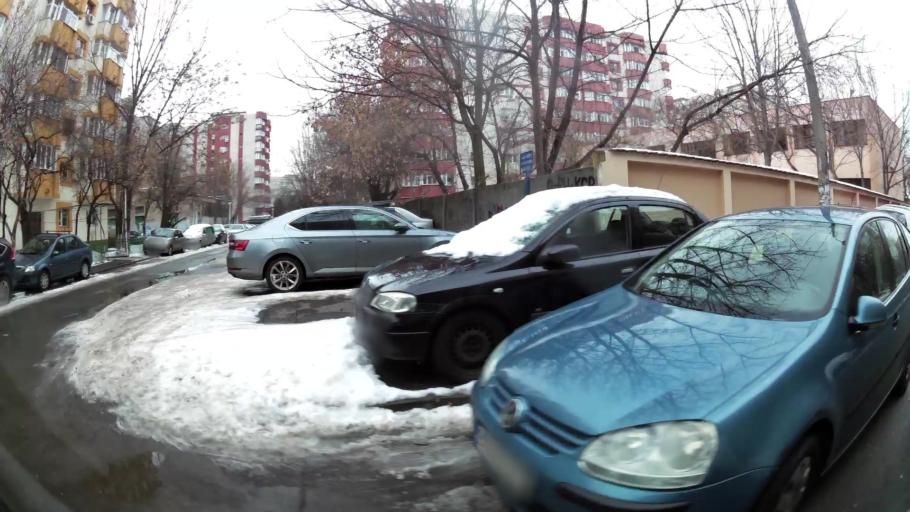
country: RO
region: Bucuresti
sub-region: Municipiul Bucuresti
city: Bucuresti
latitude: 44.4155
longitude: 26.0661
